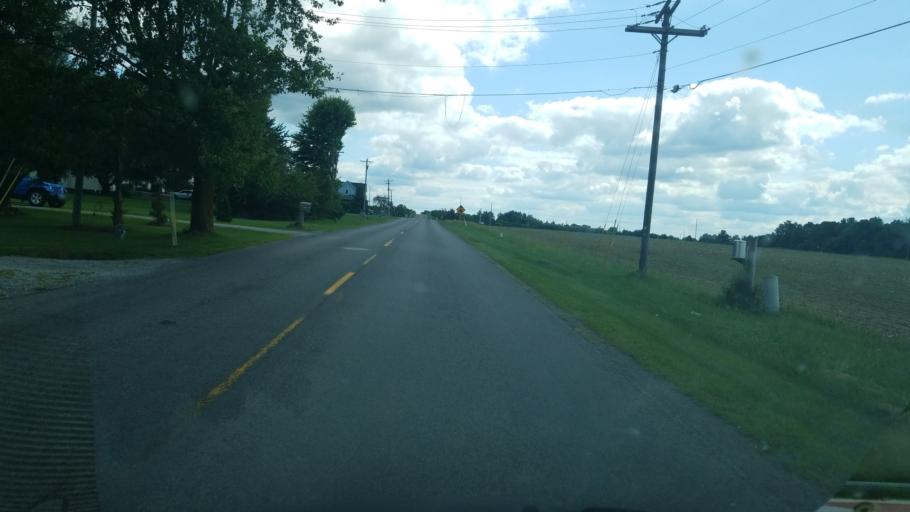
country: US
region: Ohio
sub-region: Allen County
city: Lima
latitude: 40.7769
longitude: -84.0706
